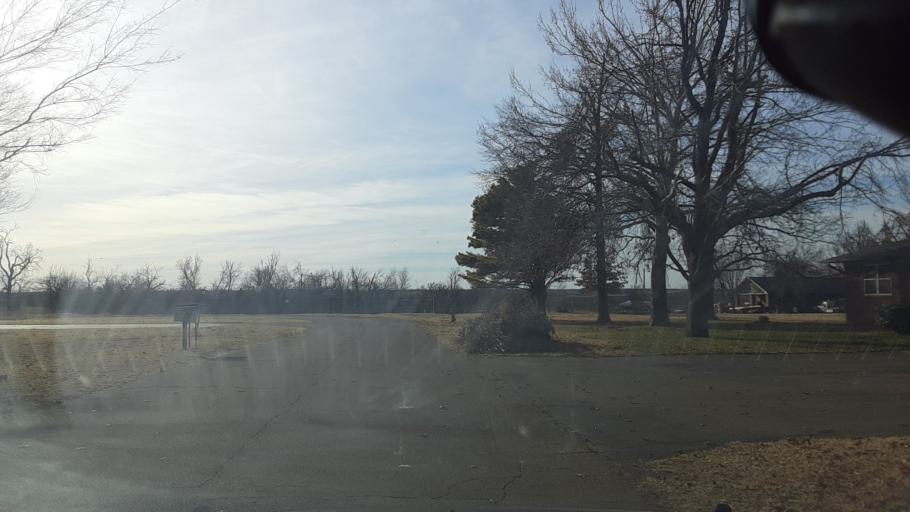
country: US
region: Oklahoma
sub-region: Logan County
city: Guthrie
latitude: 35.8532
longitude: -97.4331
